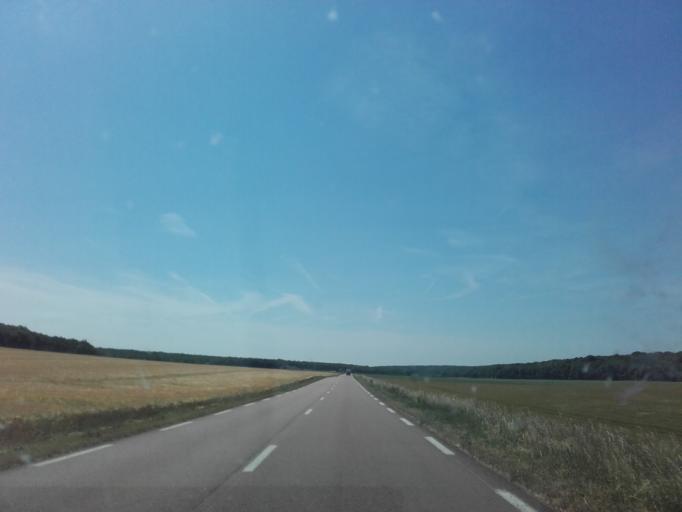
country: FR
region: Bourgogne
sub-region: Departement de l'Yonne
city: Chablis
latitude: 47.7697
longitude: 3.8141
